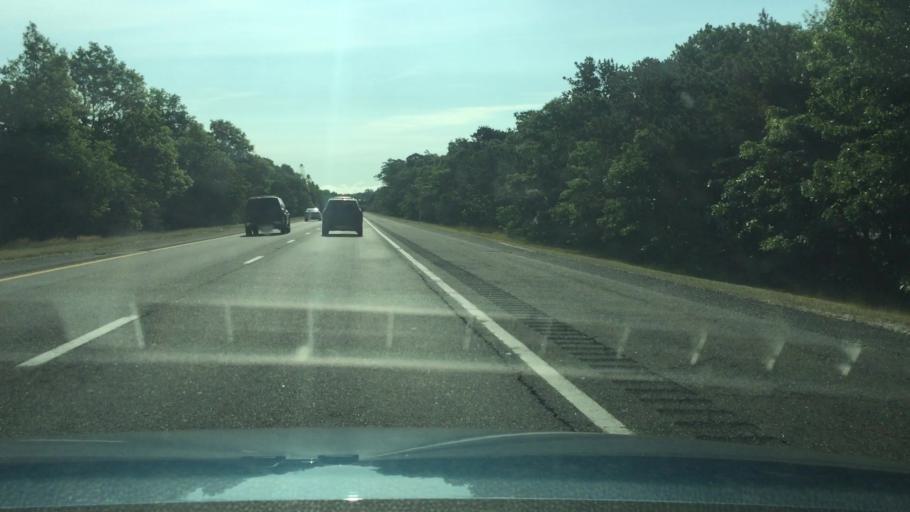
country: US
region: Massachusetts
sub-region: Barnstable County
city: South Yarmouth
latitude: 41.6914
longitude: -70.1907
